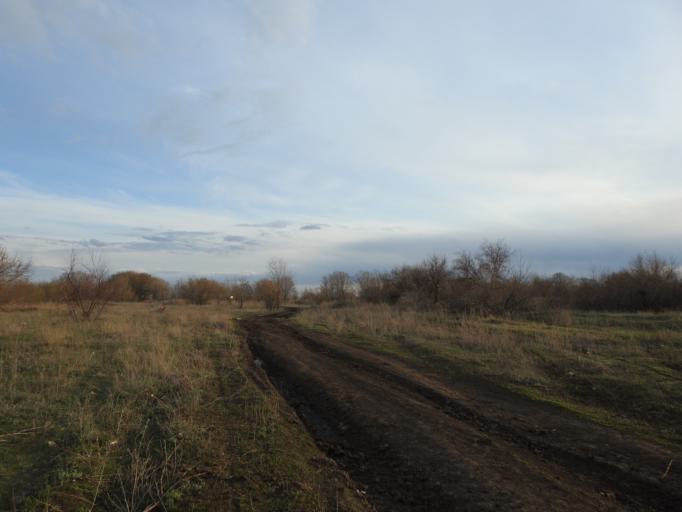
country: RU
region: Saratov
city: Engel's
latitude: 51.4279
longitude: 46.1814
